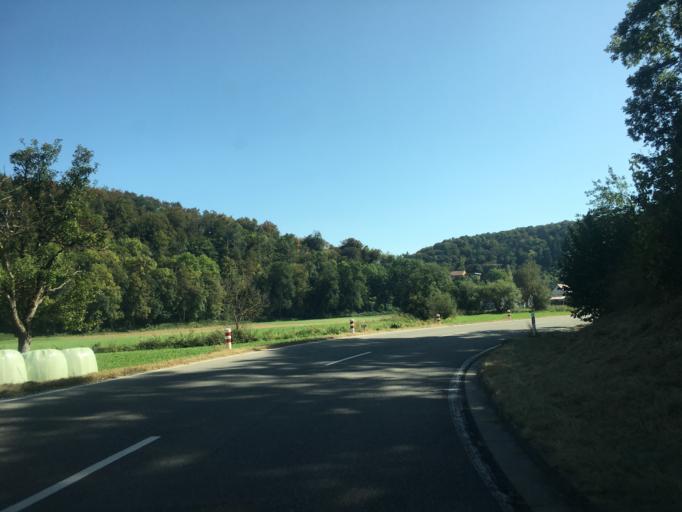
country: DE
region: Baden-Wuerttemberg
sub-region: Tuebingen Region
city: Hayingen
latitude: 48.2969
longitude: 9.4932
